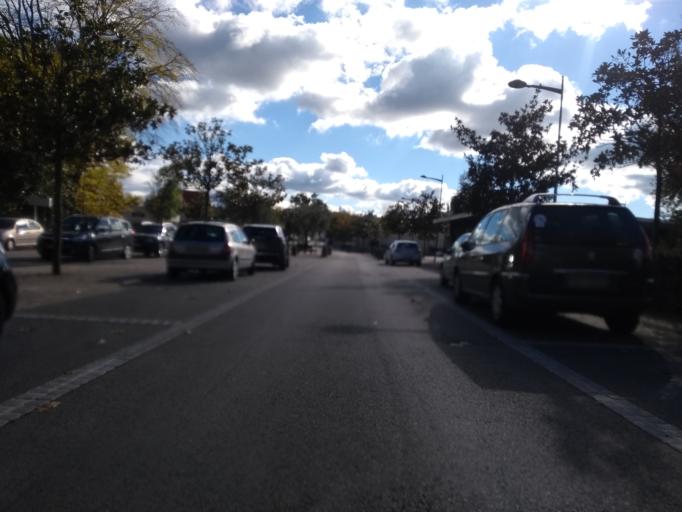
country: FR
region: Aquitaine
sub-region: Departement de la Gironde
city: Pessac
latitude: 44.8028
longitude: -0.6316
